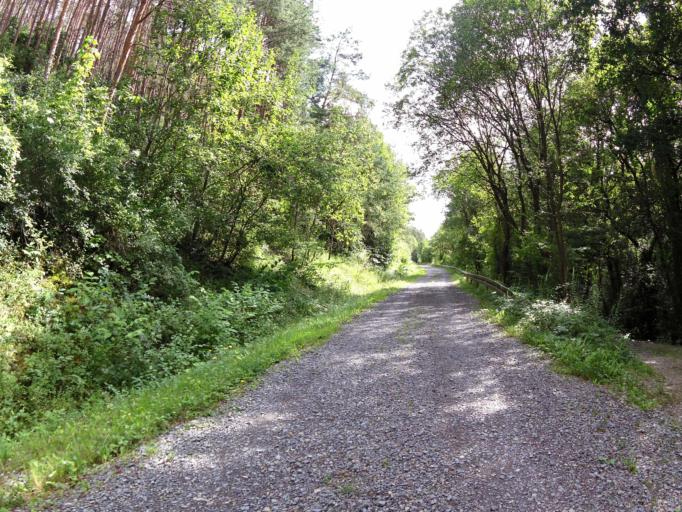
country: DE
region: Bavaria
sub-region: Regierungsbezirk Unterfranken
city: Erlabrunn
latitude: 49.8410
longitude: 9.8412
